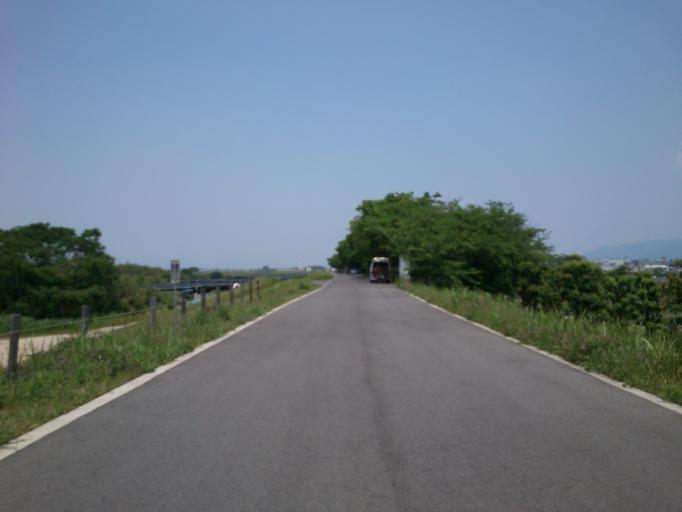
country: JP
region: Kyoto
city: Tanabe
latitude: 34.8548
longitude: 135.7547
